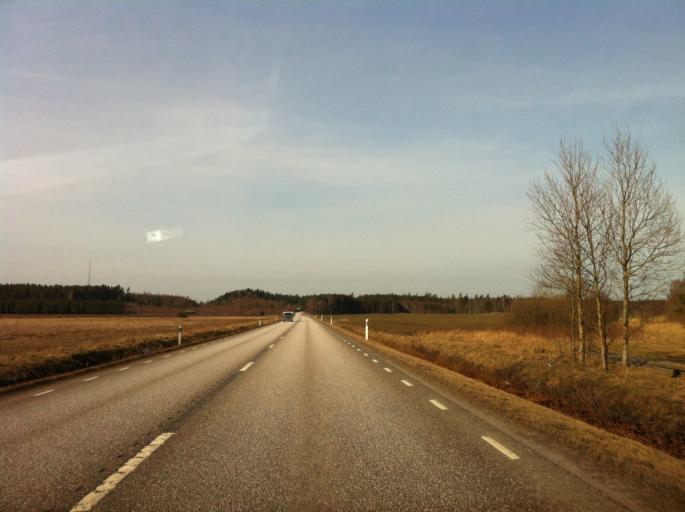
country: SE
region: Vaestra Goetaland
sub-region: Skovde Kommun
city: Skultorp
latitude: 58.2356
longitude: 13.8303
